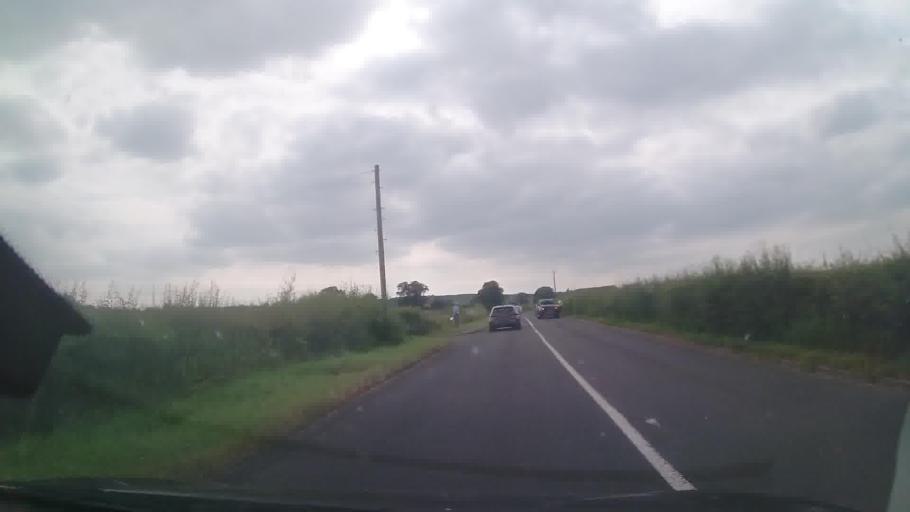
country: GB
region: England
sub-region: Staffordshire
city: Standon
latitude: 52.9431
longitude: -2.3470
